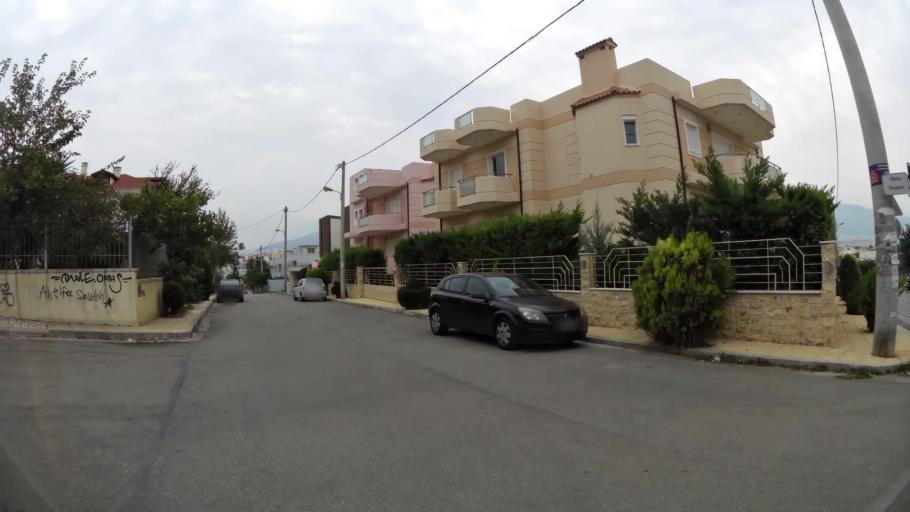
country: GR
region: Attica
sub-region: Nomarchia Athinas
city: Alimos
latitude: 37.9109
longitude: 23.7307
